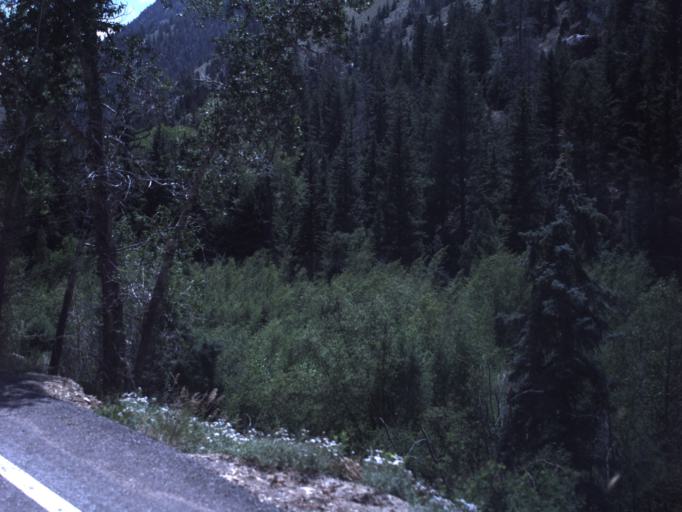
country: US
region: Utah
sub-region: Emery County
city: Huntington
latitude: 39.4522
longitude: -111.1409
